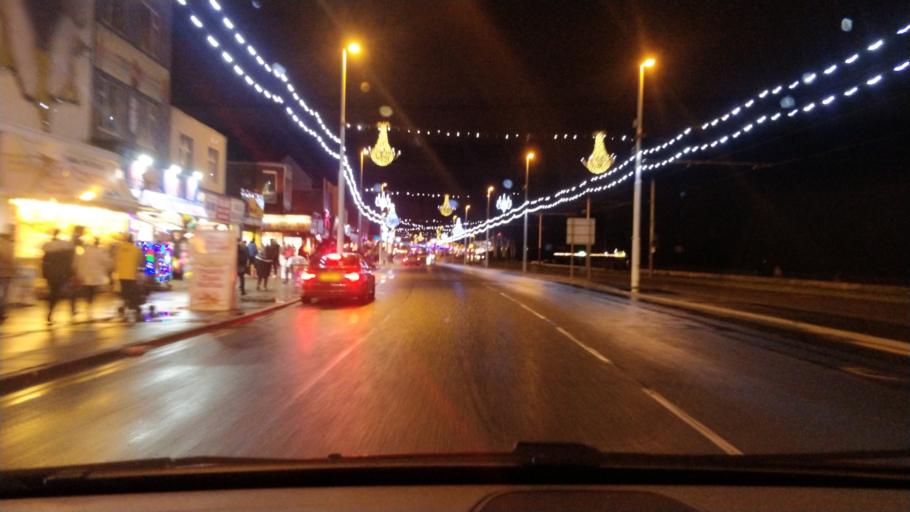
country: GB
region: England
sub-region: Blackpool
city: Blackpool
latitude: 53.8102
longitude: -3.0556
